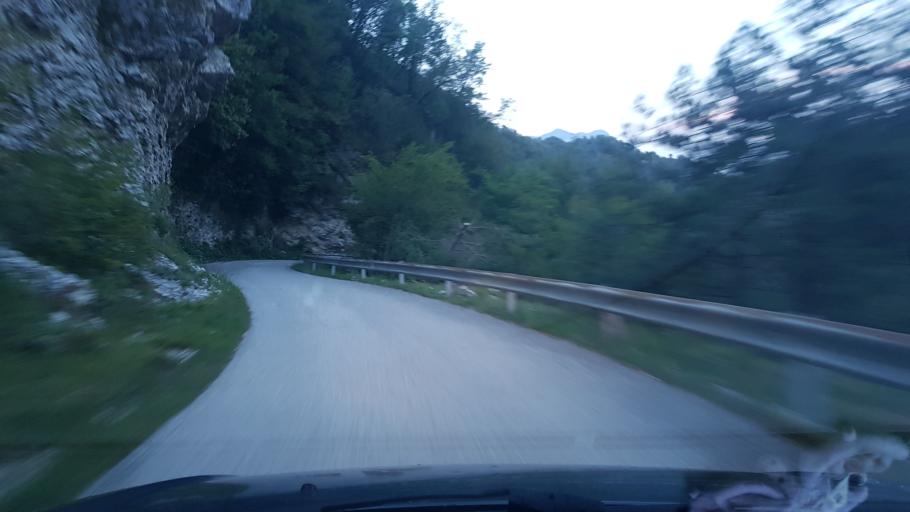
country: IT
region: Friuli Venezia Giulia
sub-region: Provincia di Pordenone
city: Frisanco
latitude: 46.2541
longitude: 12.7082
